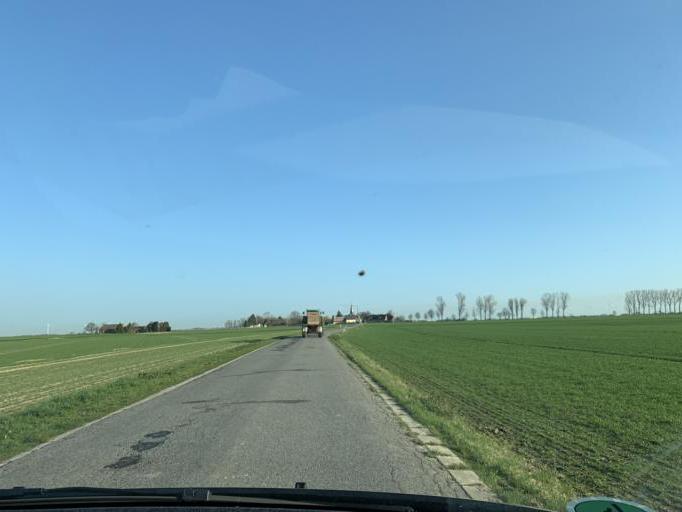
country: DE
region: North Rhine-Westphalia
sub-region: Regierungsbezirk Koln
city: Titz
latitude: 50.9817
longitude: 6.4626
